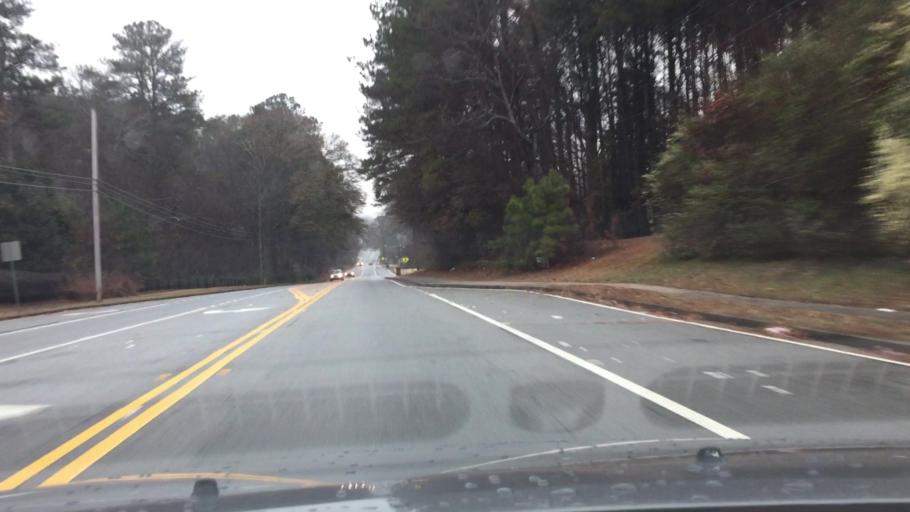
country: US
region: Georgia
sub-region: Cobb County
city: Powder Springs
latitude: 33.8892
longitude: -84.6763
